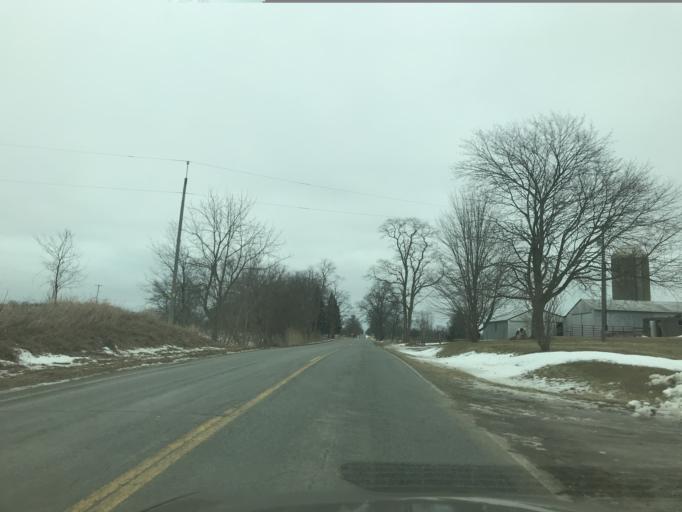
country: US
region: Michigan
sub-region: Jackson County
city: Brooklyn
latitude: 42.0734
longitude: -84.3518
